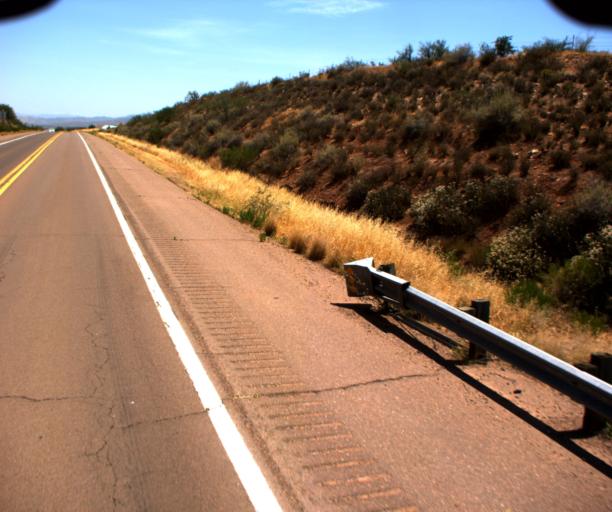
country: US
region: Arizona
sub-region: Gila County
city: Tonto Basin
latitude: 33.8648
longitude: -111.3142
